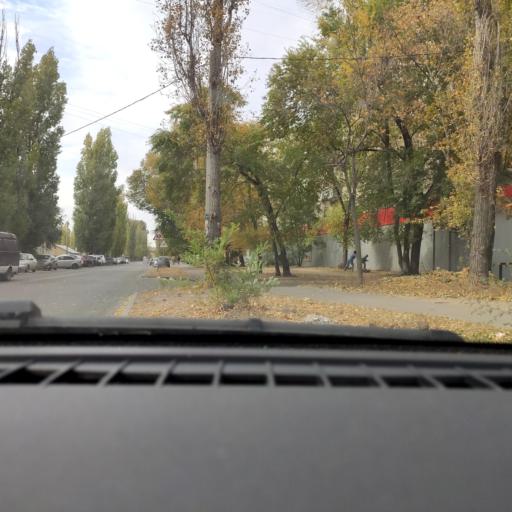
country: RU
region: Voronezj
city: Voronezh
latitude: 51.6796
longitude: 39.2702
